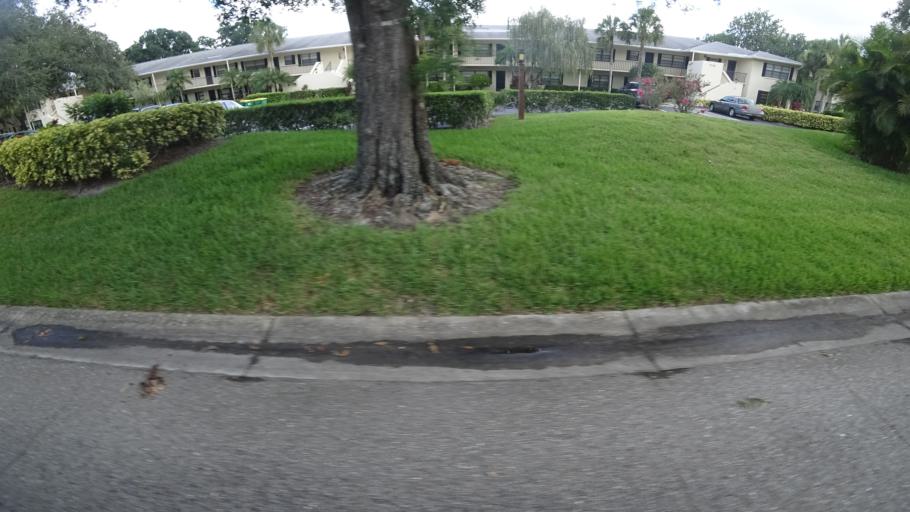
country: US
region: Florida
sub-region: Sarasota County
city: Desoto Lakes
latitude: 27.4142
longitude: -82.4934
